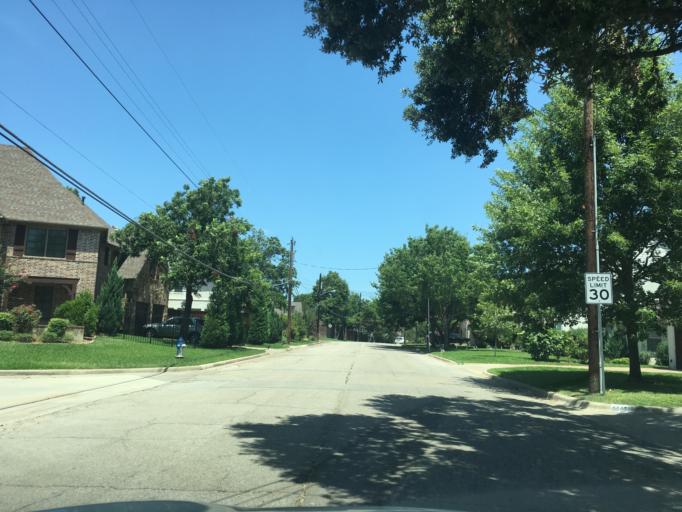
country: US
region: Texas
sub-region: Dallas County
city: Highland Park
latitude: 32.8418
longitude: -96.7390
